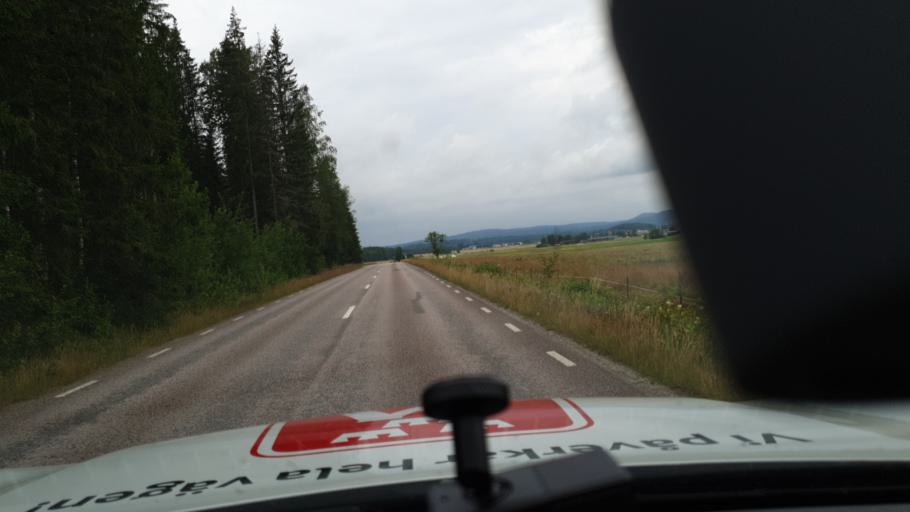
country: SE
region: Vaermland
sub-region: Sunne Kommun
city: Sunne
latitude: 59.8254
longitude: 13.1955
